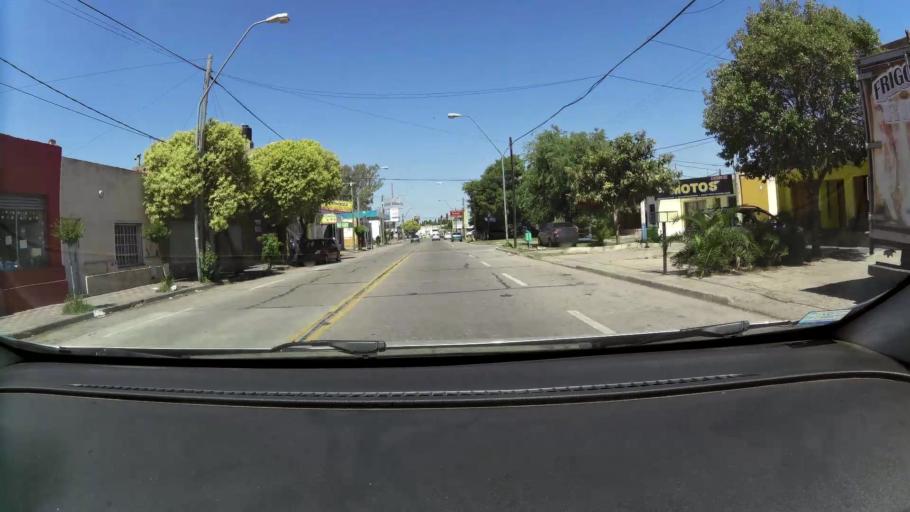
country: AR
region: Cordoba
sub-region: Departamento de Capital
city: Cordoba
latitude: -31.3794
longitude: -64.1490
